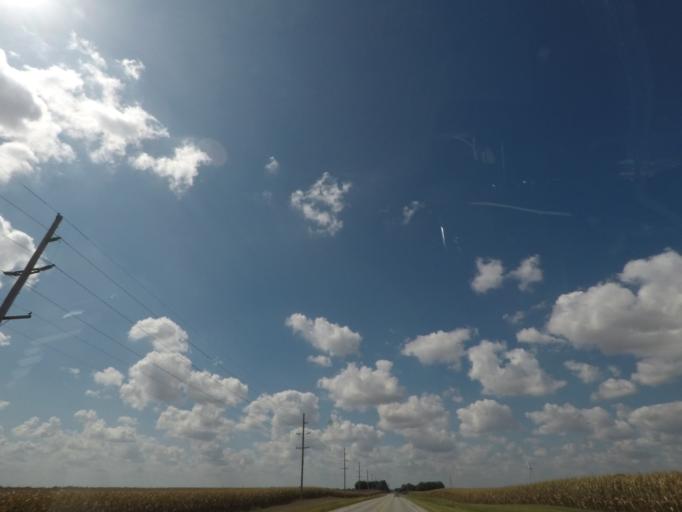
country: US
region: Iowa
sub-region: Story County
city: Nevada
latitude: 42.0226
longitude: -93.4079
